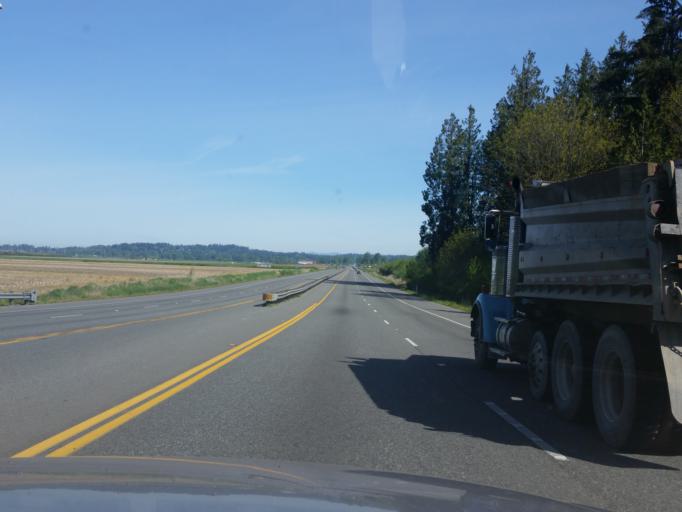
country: US
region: Washington
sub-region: Snohomish County
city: Cathcart
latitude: 47.8793
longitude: -122.1098
